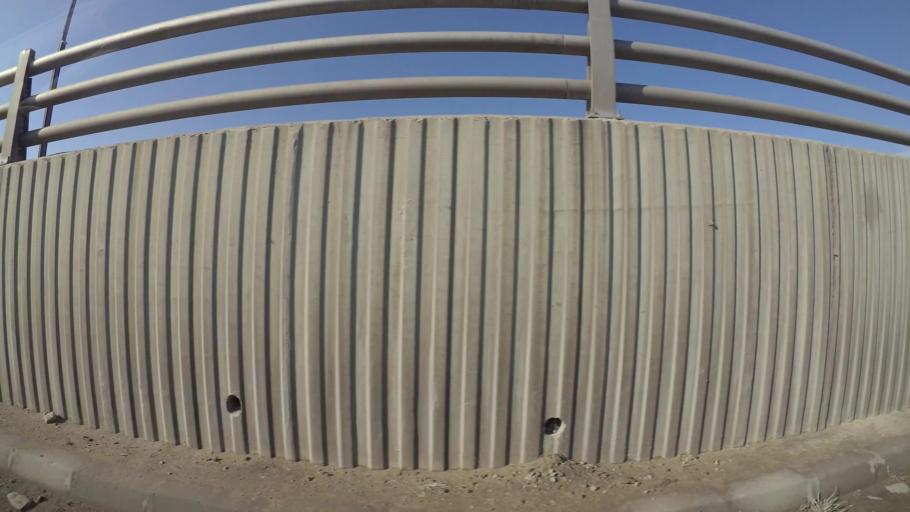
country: JO
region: Amman
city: Al Jubayhah
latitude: 32.0628
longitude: 35.8397
